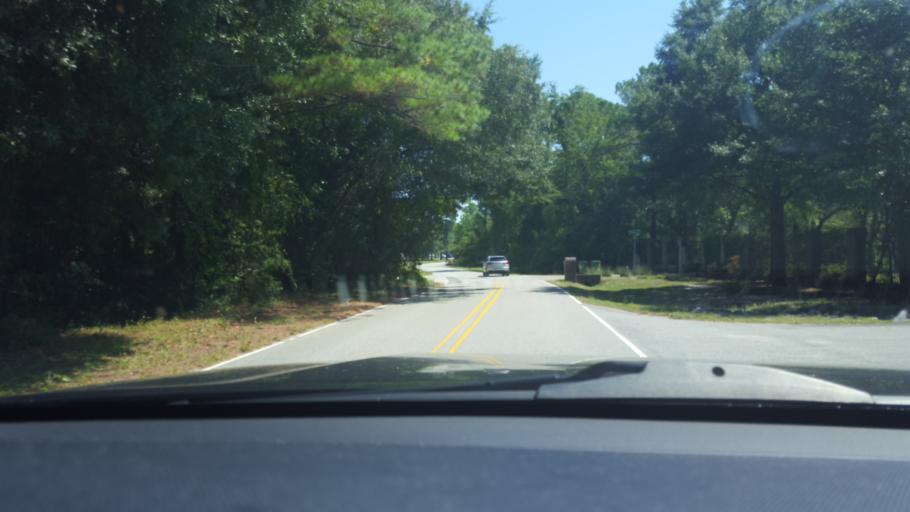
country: US
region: North Carolina
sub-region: New Hanover County
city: Ogden
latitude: 34.2558
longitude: -77.8299
